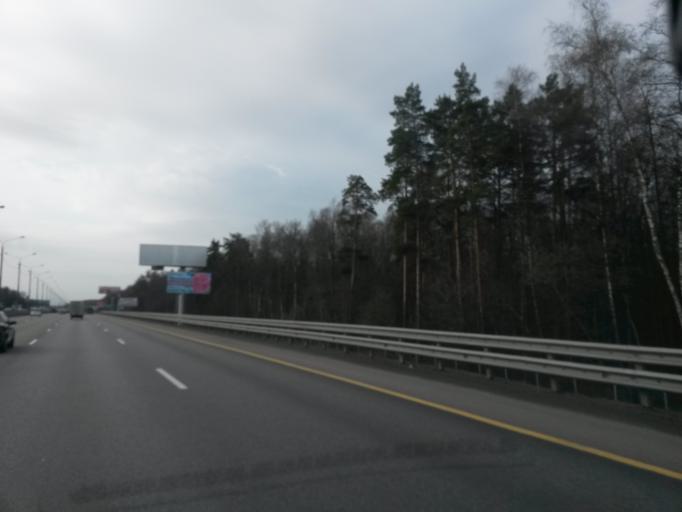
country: RU
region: Moskovskaya
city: Shcherbinka
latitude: 55.5129
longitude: 37.6081
